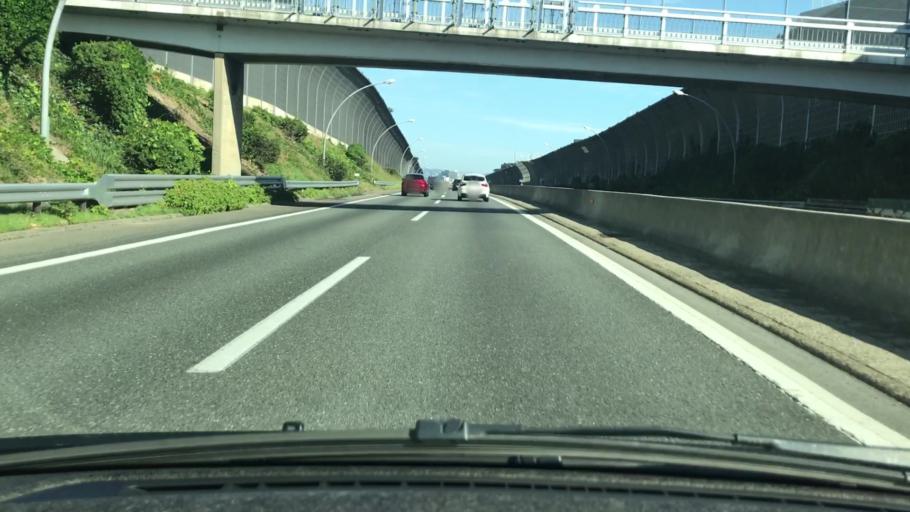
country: JP
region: Osaka
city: Suita
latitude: 34.7767
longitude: 135.5207
